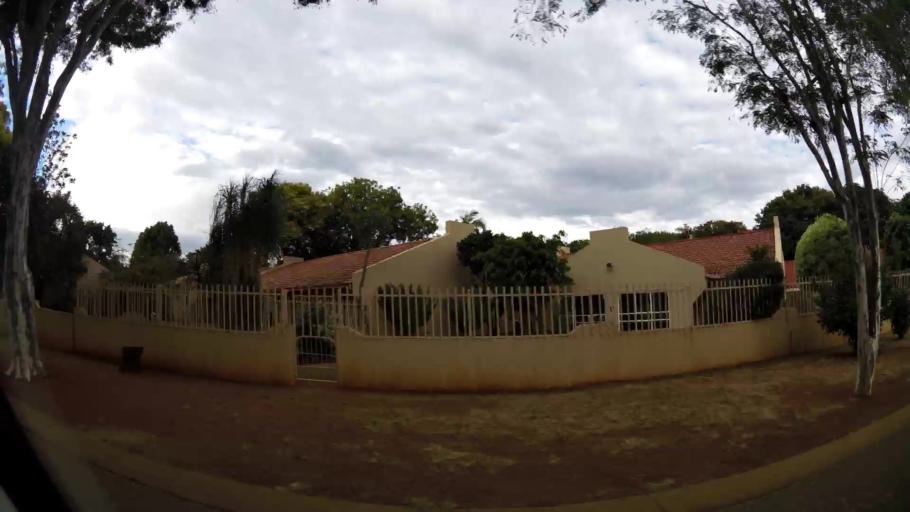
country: ZA
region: Limpopo
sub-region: Waterberg District Municipality
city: Modimolle
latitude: -24.5100
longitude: 28.7158
